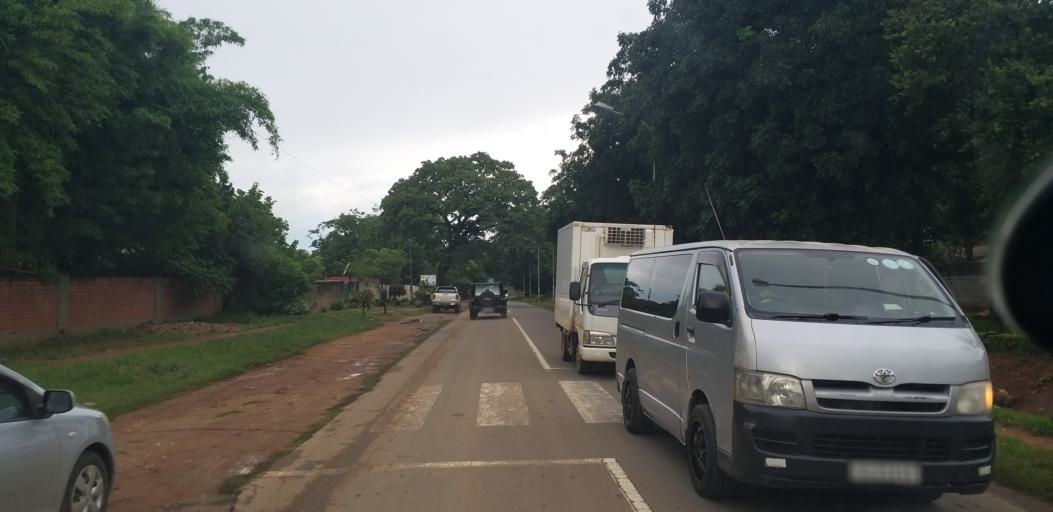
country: ZM
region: Lusaka
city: Lusaka
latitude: -15.4305
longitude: 28.3440
